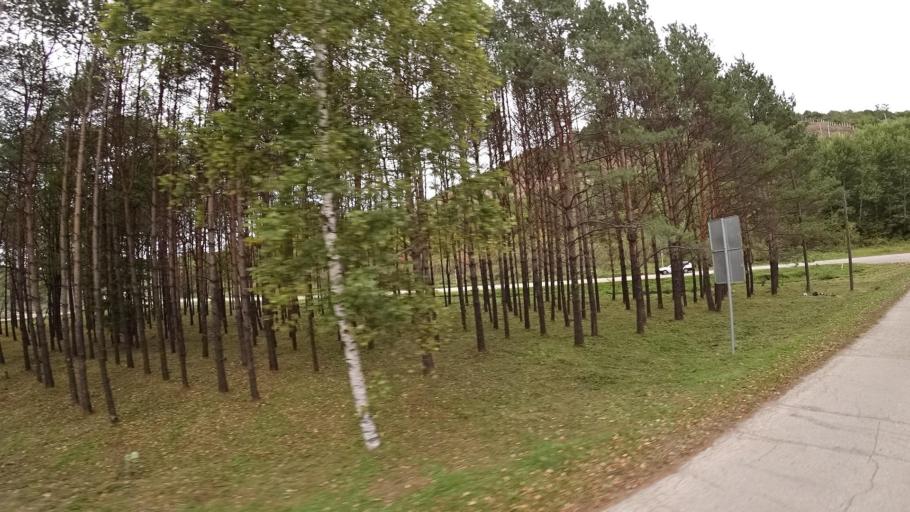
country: RU
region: Jewish Autonomous Oblast
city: Khingansk
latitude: 48.9873
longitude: 131.0607
